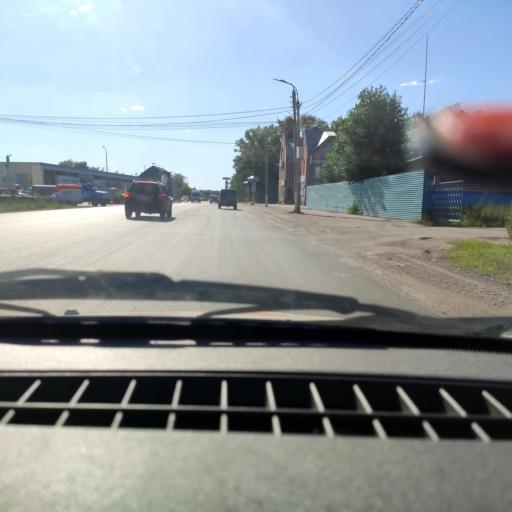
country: RU
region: Bashkortostan
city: Sterlitamak
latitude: 53.6543
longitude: 55.9582
